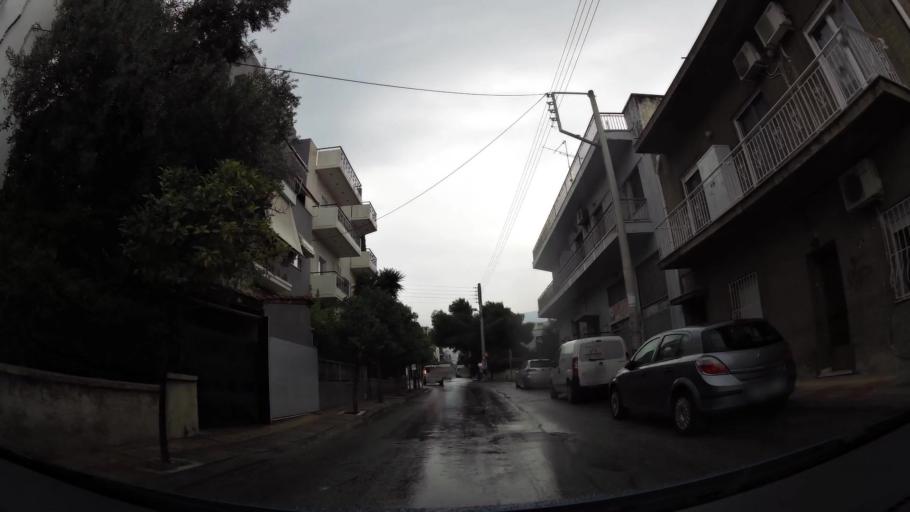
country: GR
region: Attica
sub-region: Nomarchia Athinas
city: Ymittos
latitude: 37.9544
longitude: 23.7493
